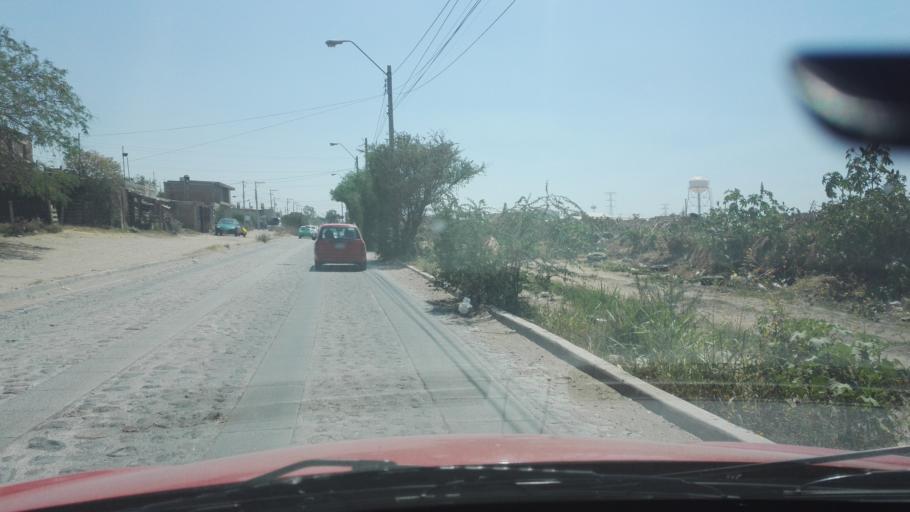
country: MX
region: Guanajuato
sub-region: Leon
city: Fraccionamiento Paraiso Real
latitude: 21.0926
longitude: -101.5981
